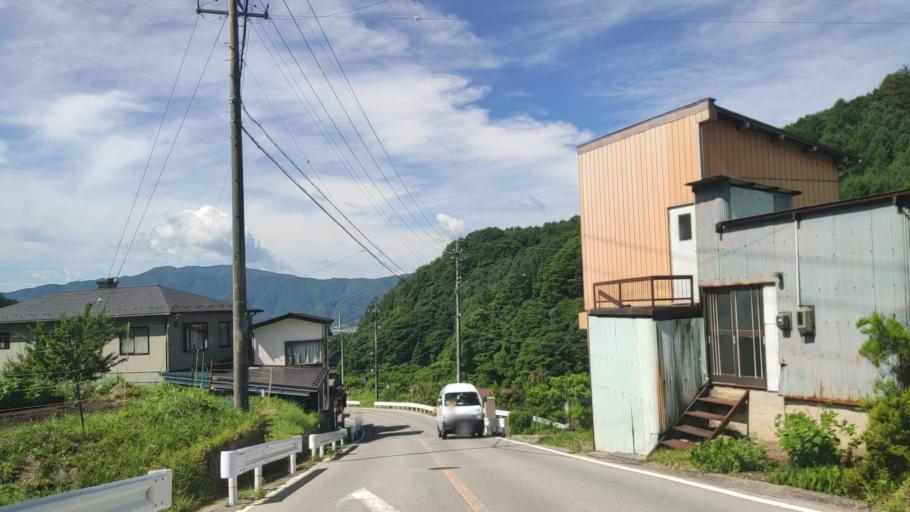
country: JP
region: Nagano
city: Suwa
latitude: 36.0552
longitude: 138.1294
